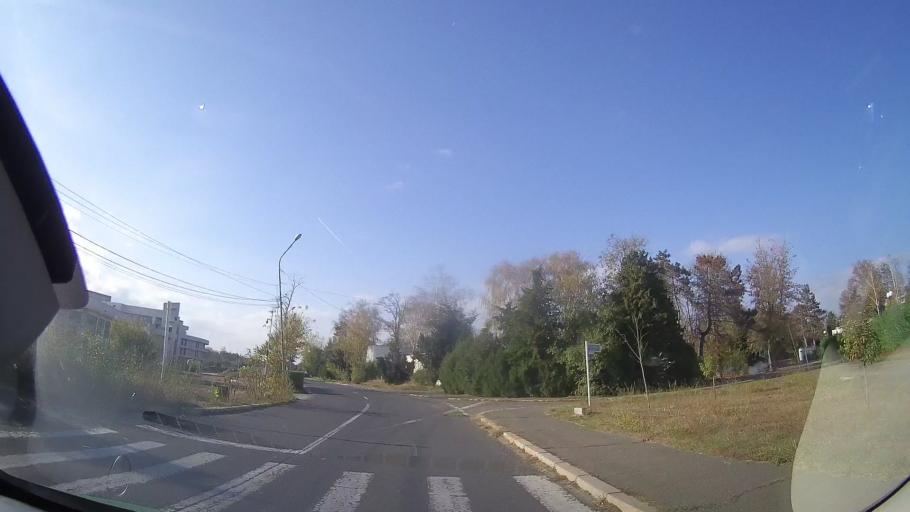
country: RO
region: Constanta
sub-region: Municipiul Mangalia
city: Mangalia
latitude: 43.8444
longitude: 28.5919
